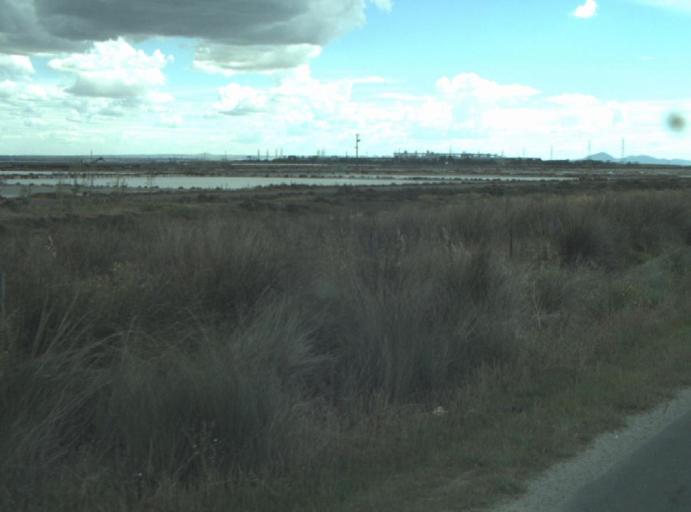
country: AU
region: Victoria
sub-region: Greater Geelong
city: Leopold
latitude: -38.1594
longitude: 144.4304
